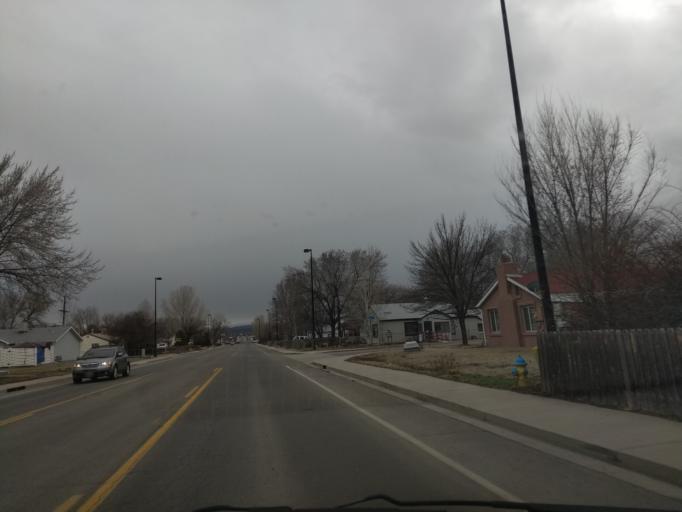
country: US
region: Colorado
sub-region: Mesa County
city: Fruitvale
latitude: 39.0809
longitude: -108.5152
